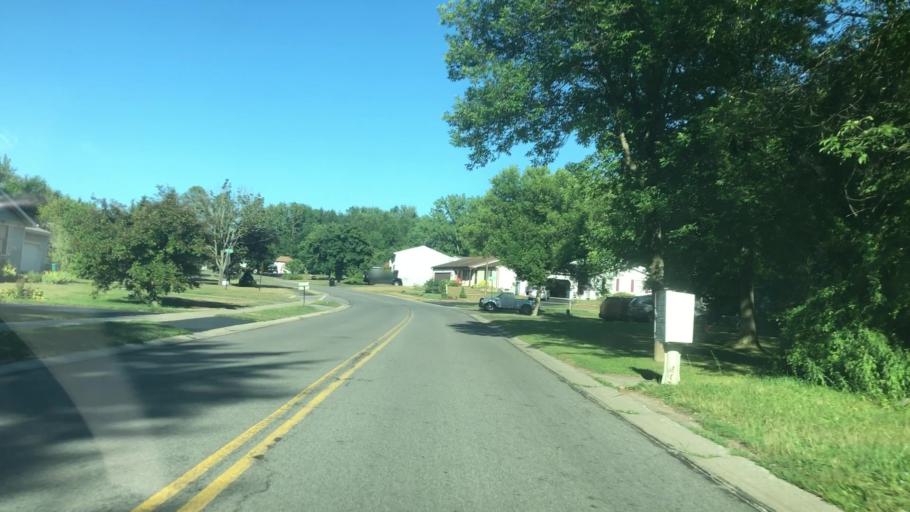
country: US
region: New York
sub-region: Wayne County
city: Macedon
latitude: 43.1239
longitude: -77.3011
